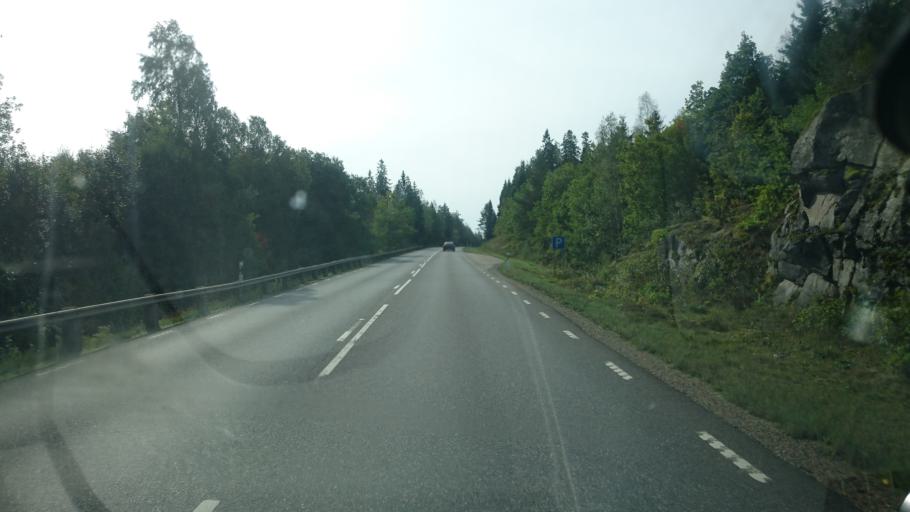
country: SE
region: Vaestra Goetaland
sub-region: Alingsas Kommun
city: Sollebrunn
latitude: 58.0381
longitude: 12.4660
